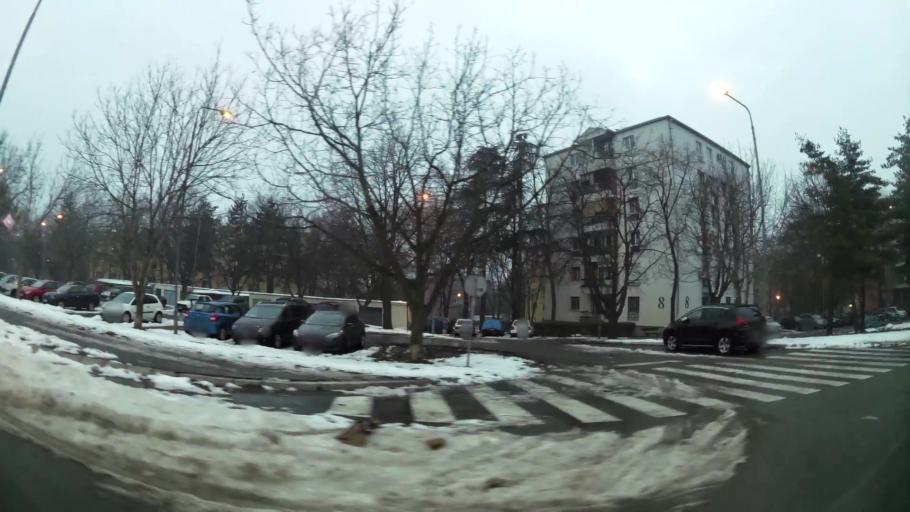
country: RS
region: Central Serbia
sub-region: Belgrade
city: Vozdovac
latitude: 44.7694
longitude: 20.4969
